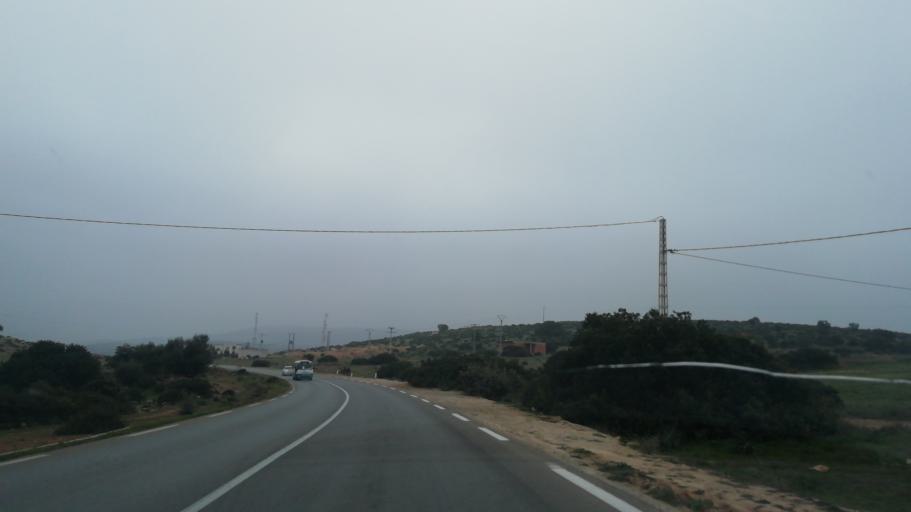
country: DZ
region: Mascara
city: Oued el Abtal
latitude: 35.2926
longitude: 0.4654
